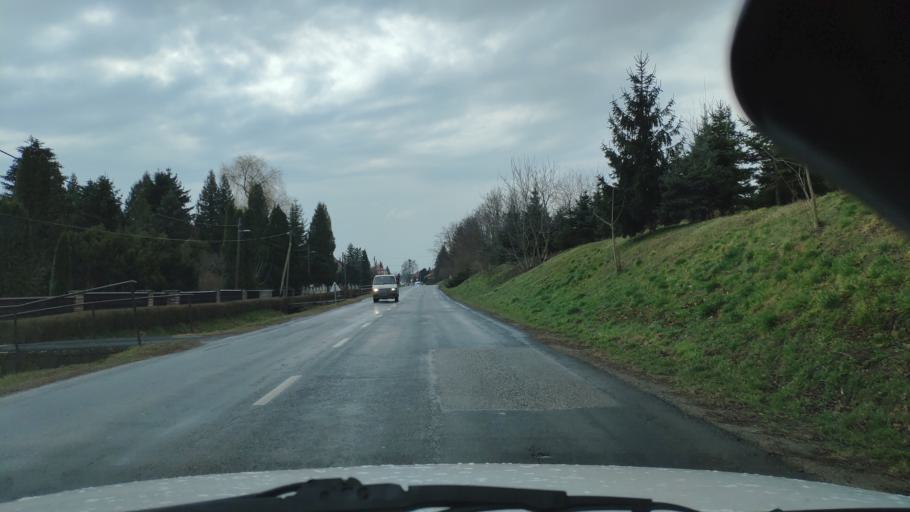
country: HU
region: Zala
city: Nagykanizsa
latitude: 46.4149
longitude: 16.9848
